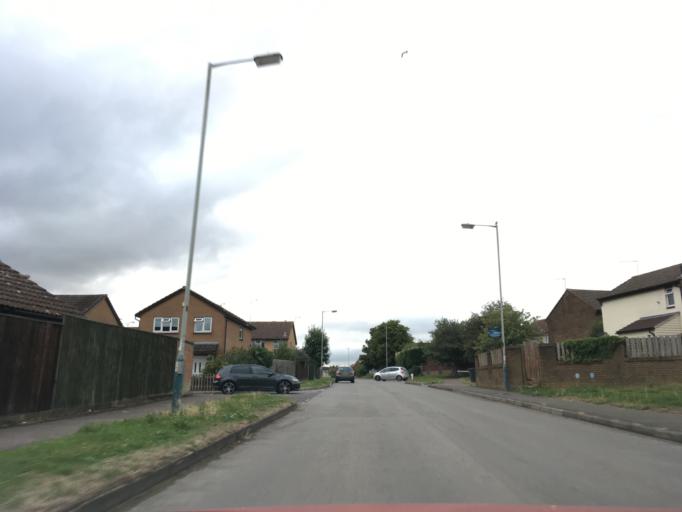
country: GB
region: England
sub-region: Wiltshire
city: Chippenham
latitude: 51.4472
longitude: -2.0972
